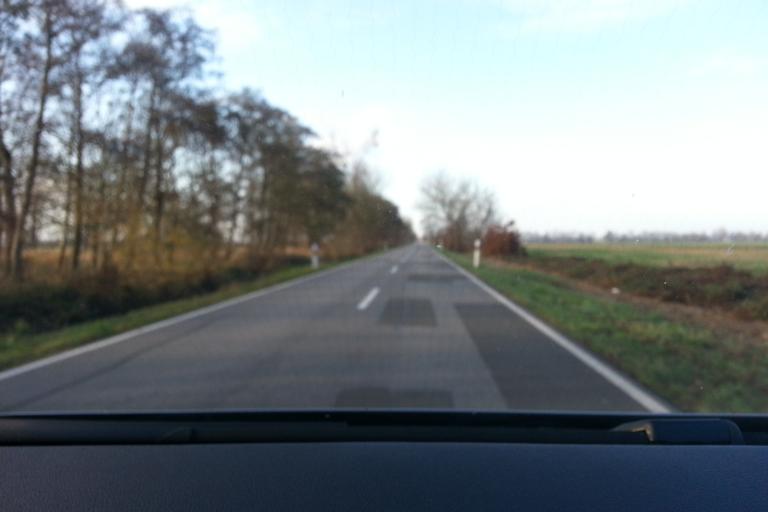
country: DE
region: Mecklenburg-Vorpommern
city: Strasburg
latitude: 53.6317
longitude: 13.7561
